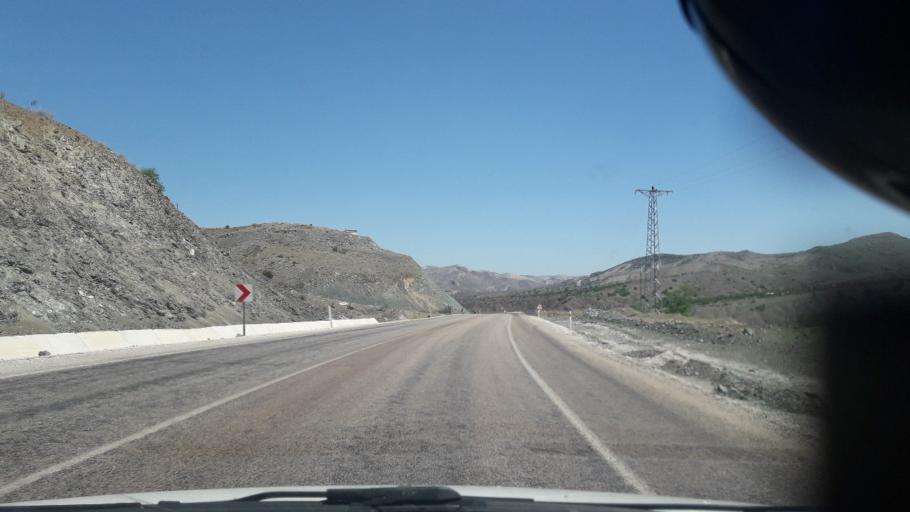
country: TR
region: Malatya
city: Hekimhan
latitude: 38.8218
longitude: 37.8780
